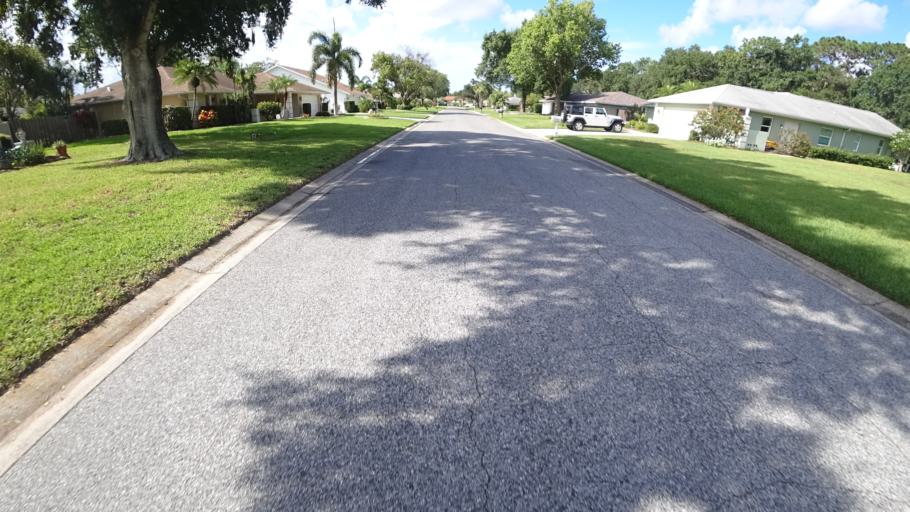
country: US
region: Florida
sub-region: Sarasota County
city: Desoto Lakes
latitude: 27.3950
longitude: -82.4886
